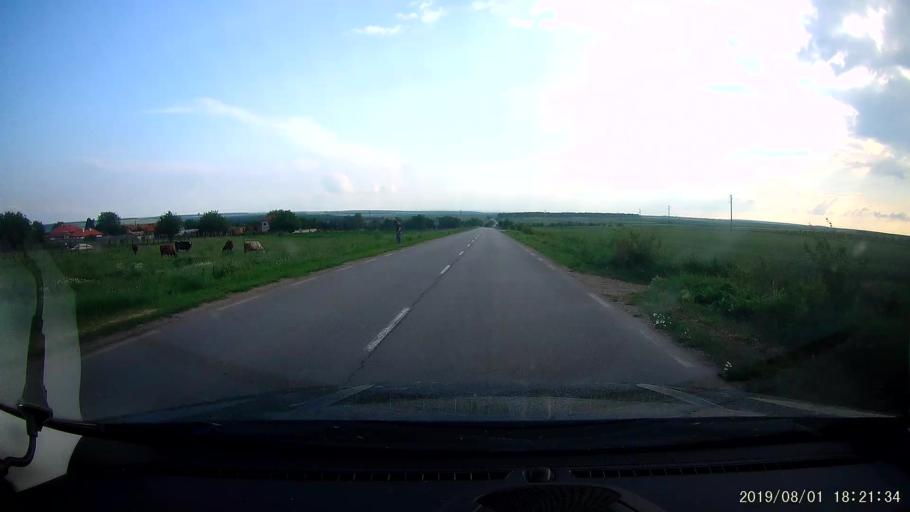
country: BG
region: Shumen
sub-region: Obshtina Kaolinovo
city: Kaolinovo
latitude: 43.6516
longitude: 27.0700
